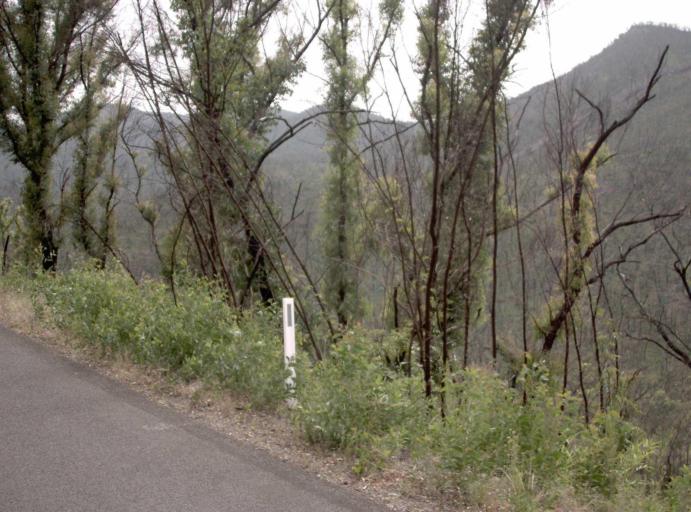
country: AU
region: Victoria
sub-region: Wellington
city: Heyfield
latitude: -37.7307
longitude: 146.6700
